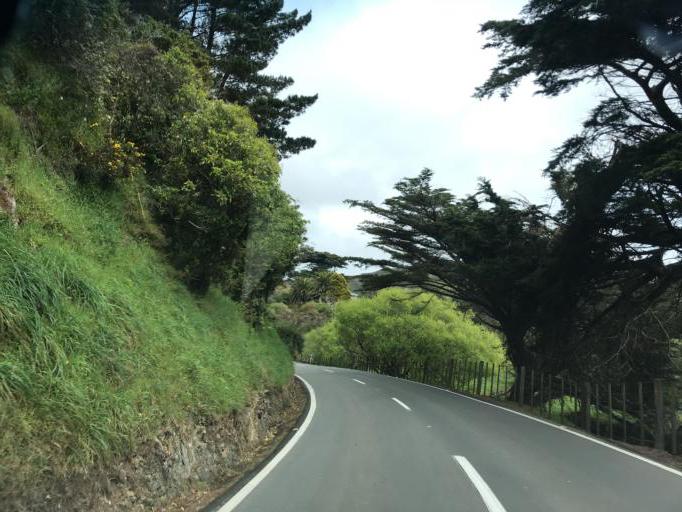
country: NZ
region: Wellington
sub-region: Wellington City
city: Kelburn
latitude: -41.2130
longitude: 174.7785
